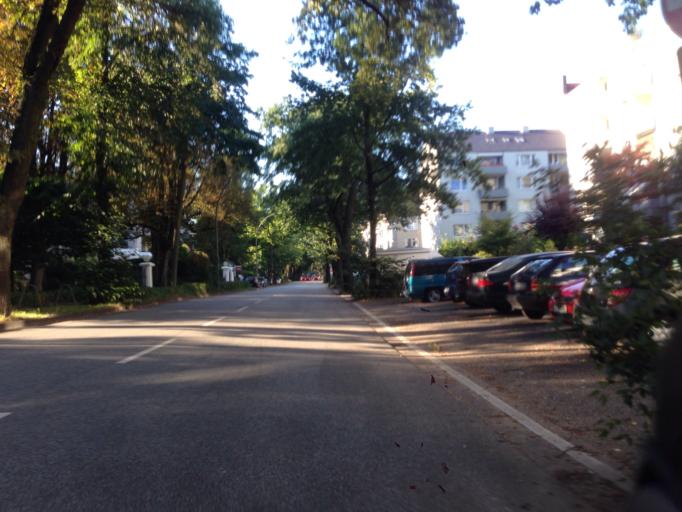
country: DE
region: Hamburg
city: Hamburg
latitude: 53.5846
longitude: 10.0048
